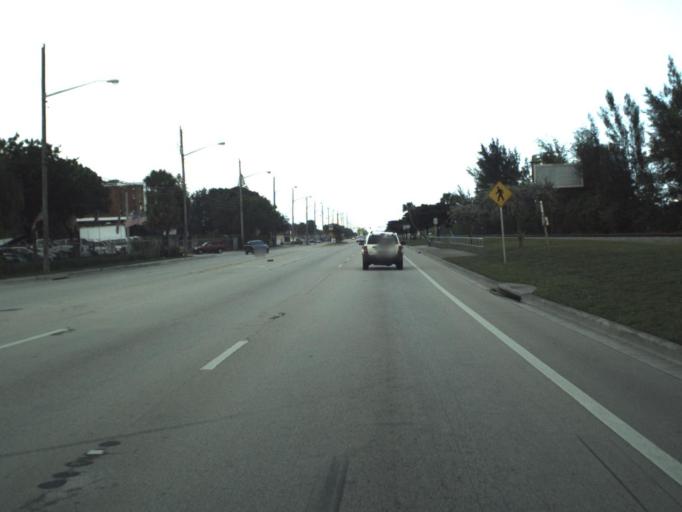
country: US
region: Florida
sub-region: Broward County
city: Pompano Beach Highlands
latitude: 26.2847
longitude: -80.1110
